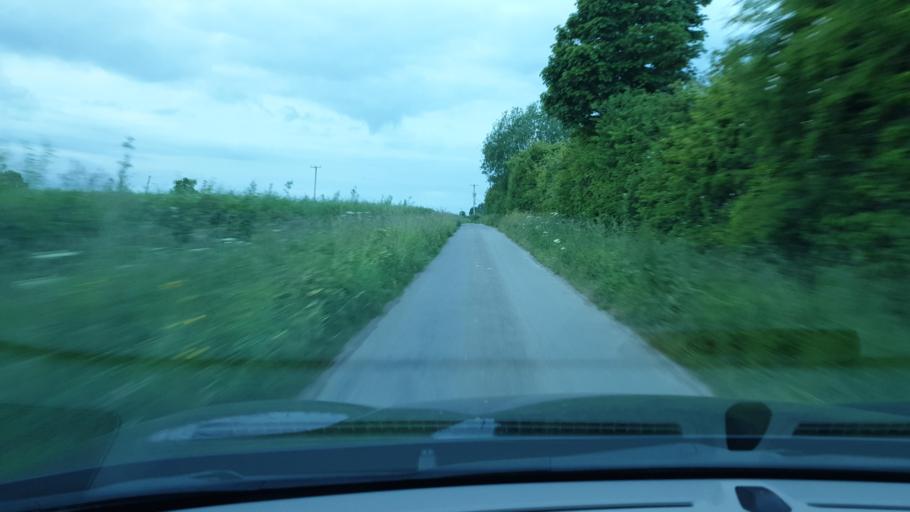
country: IE
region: Leinster
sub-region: An Mhi
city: Ashbourne
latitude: 53.5426
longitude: -6.3467
